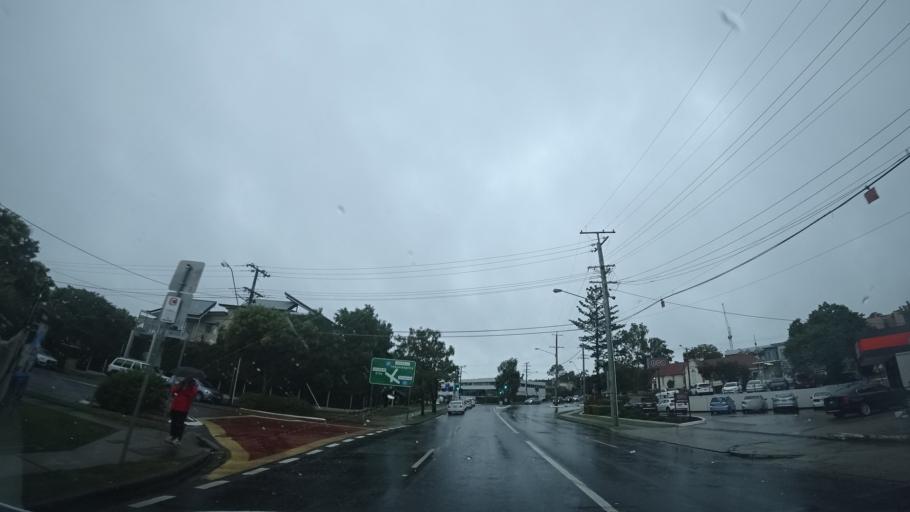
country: AU
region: Queensland
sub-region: Brisbane
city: Toowong
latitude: -27.4801
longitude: 152.9907
